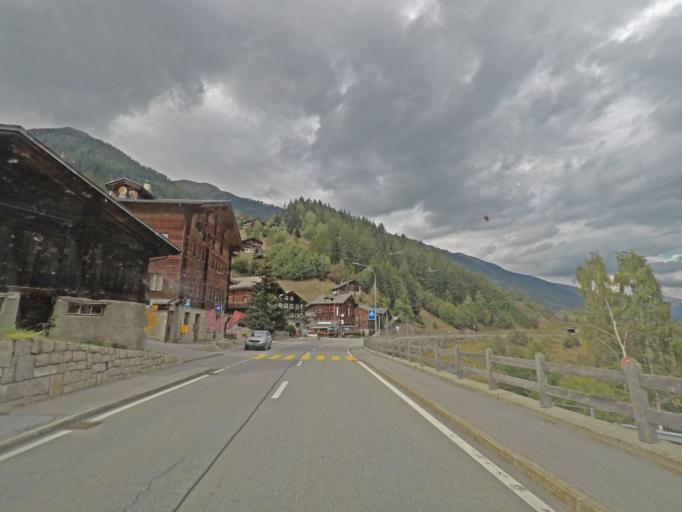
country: CH
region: Valais
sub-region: Goms District
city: Fiesch
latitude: 46.4428
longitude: 8.2028
